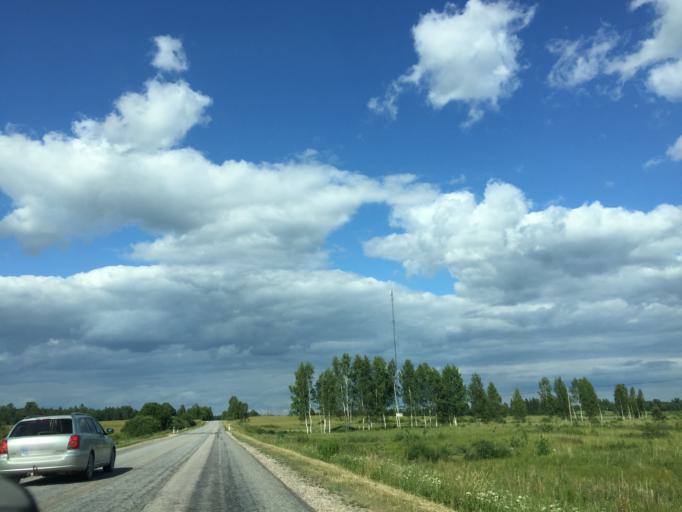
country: LV
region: Ogre
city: Jumprava
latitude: 56.7870
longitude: 25.0267
